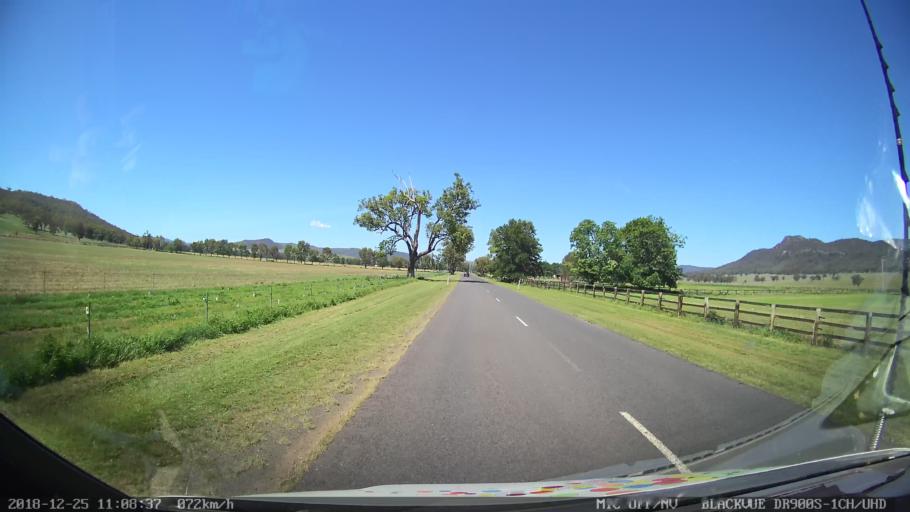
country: AU
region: New South Wales
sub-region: Upper Hunter Shire
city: Merriwa
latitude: -32.4036
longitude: 150.1233
